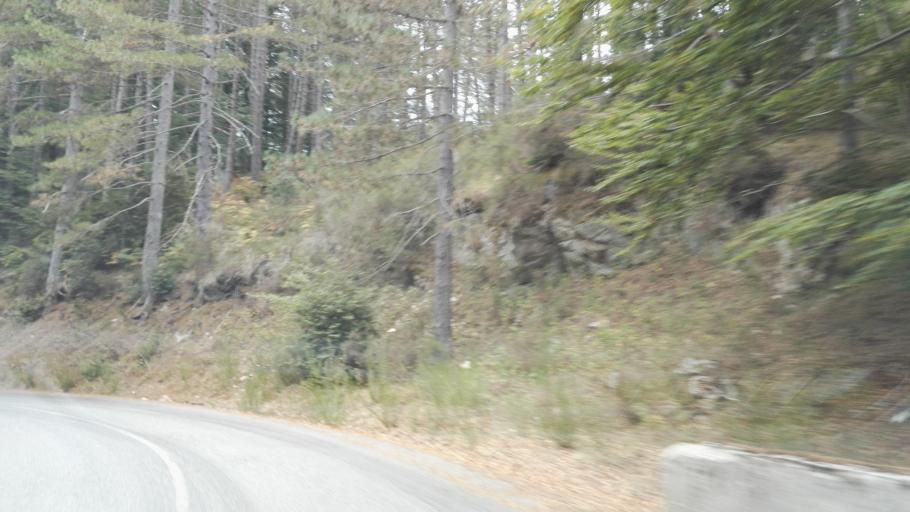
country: IT
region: Calabria
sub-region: Provincia di Vibo-Valentia
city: Nardodipace
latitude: 38.4945
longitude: 16.3446
